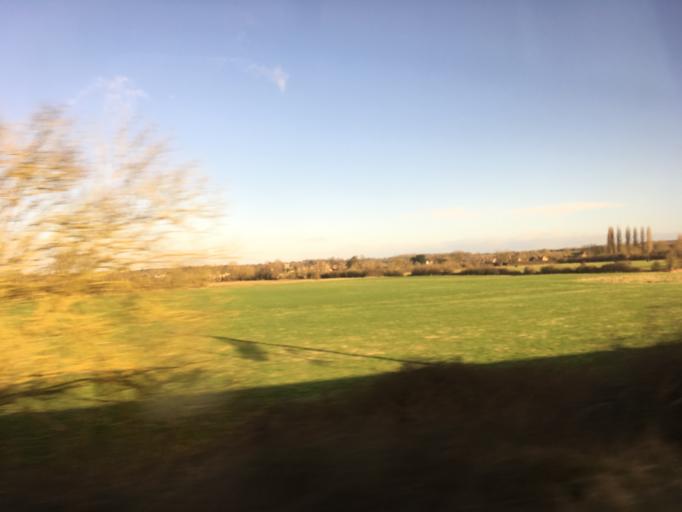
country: GB
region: England
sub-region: Borough of Swindon
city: Wanborough
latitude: 51.5818
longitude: -1.7183
